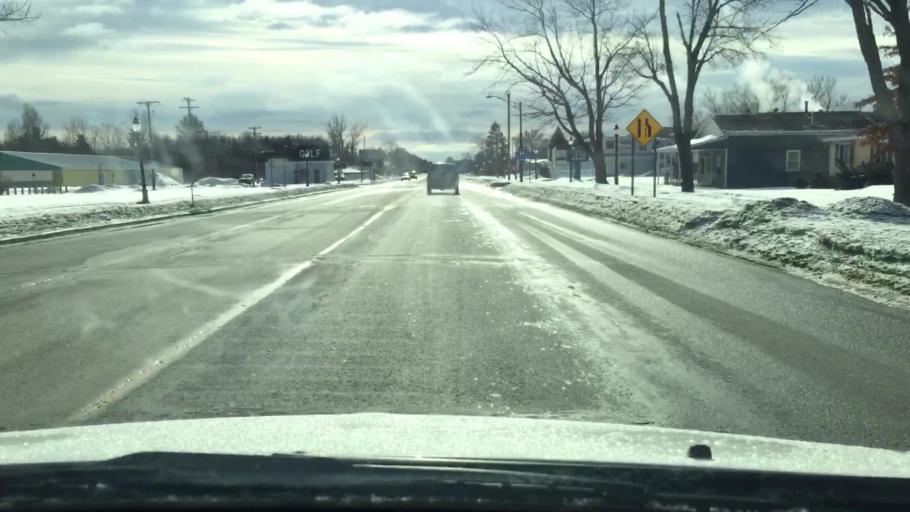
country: US
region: Michigan
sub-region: Kalkaska County
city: Kalkaska
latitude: 44.7295
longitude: -85.1795
